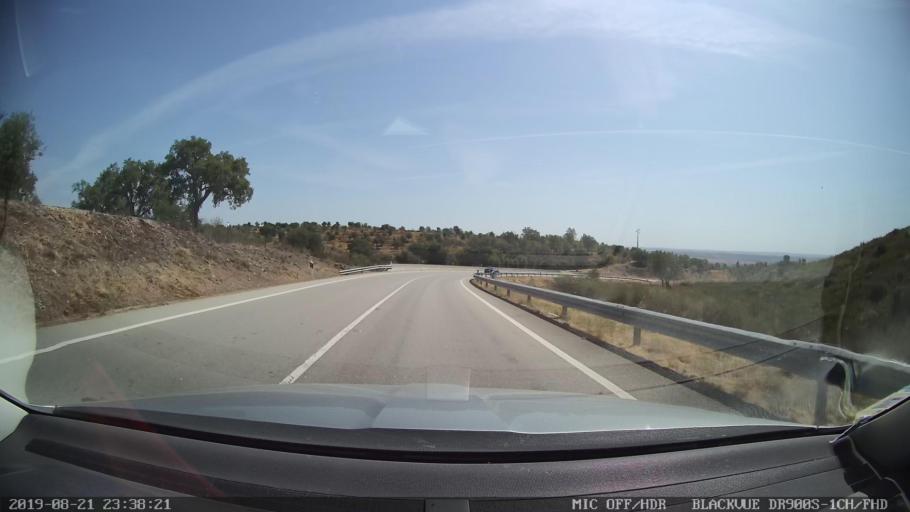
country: PT
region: Guarda
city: Alcains
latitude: 39.8613
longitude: -7.3524
